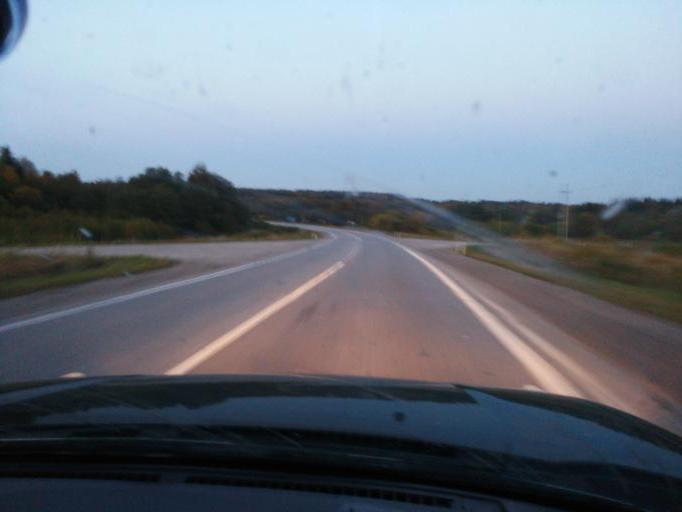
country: RU
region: Perm
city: Verkhnechusovskiye Gorodki
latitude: 58.2645
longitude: 57.3350
